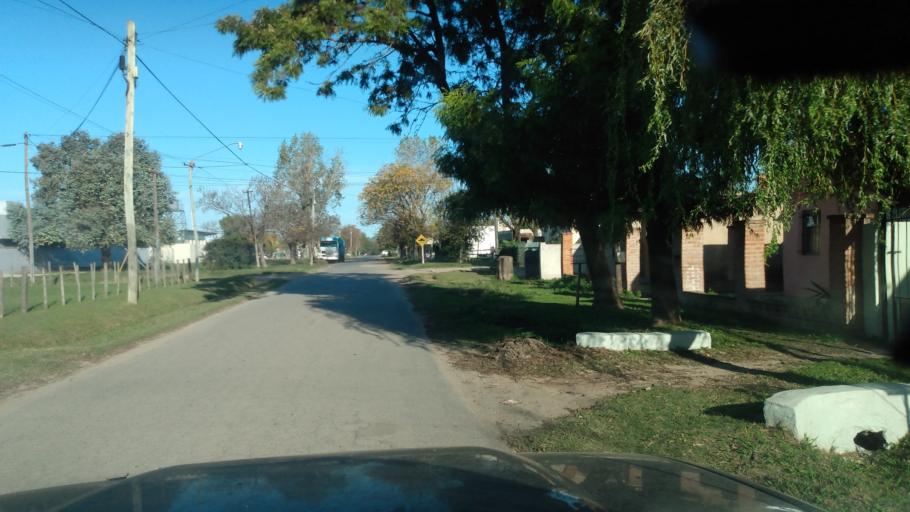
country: AR
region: Buenos Aires
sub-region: Partido de Lujan
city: Lujan
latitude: -34.5417
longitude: -59.1192
